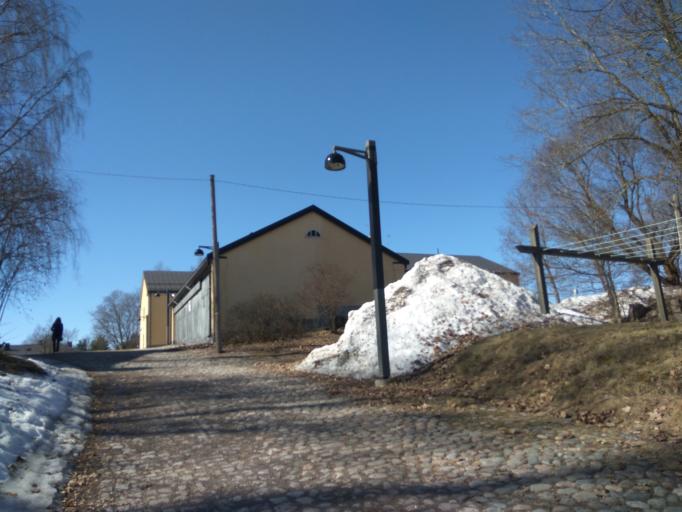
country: FI
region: South Karelia
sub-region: Lappeenranta
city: Lappeenranta
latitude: 61.0661
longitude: 28.1851
